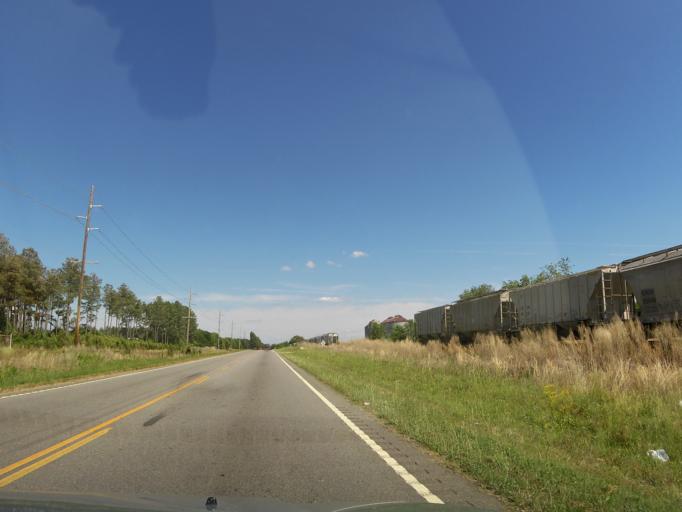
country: US
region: South Carolina
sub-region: Aiken County
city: Aiken
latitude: 33.5426
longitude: -81.6707
